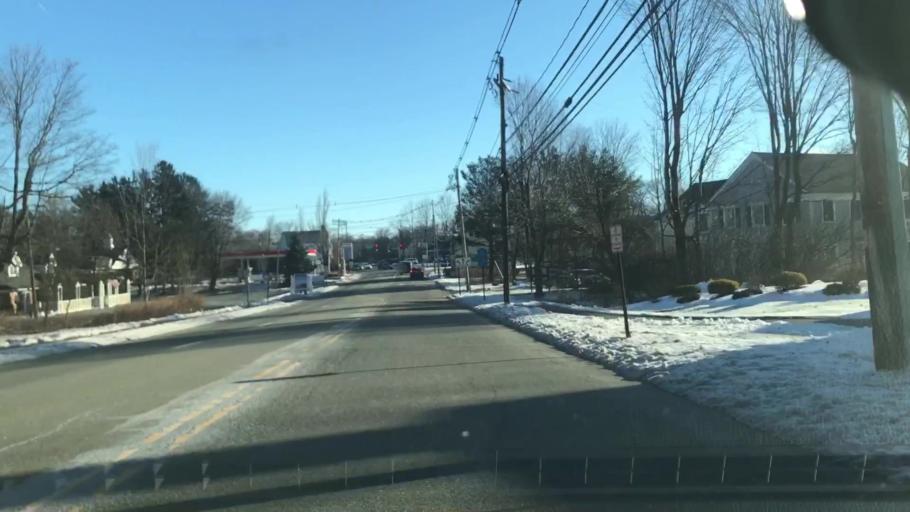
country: US
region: New Jersey
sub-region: Morris County
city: Chester
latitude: 40.7884
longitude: -74.6834
